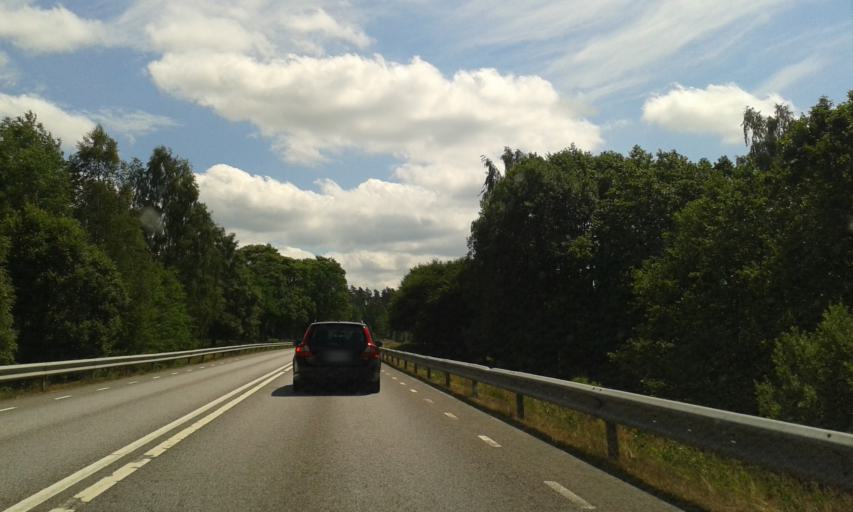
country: SE
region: Joenkoeping
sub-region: Varnamo Kommun
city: Rydaholm
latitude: 56.9706
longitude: 14.3294
